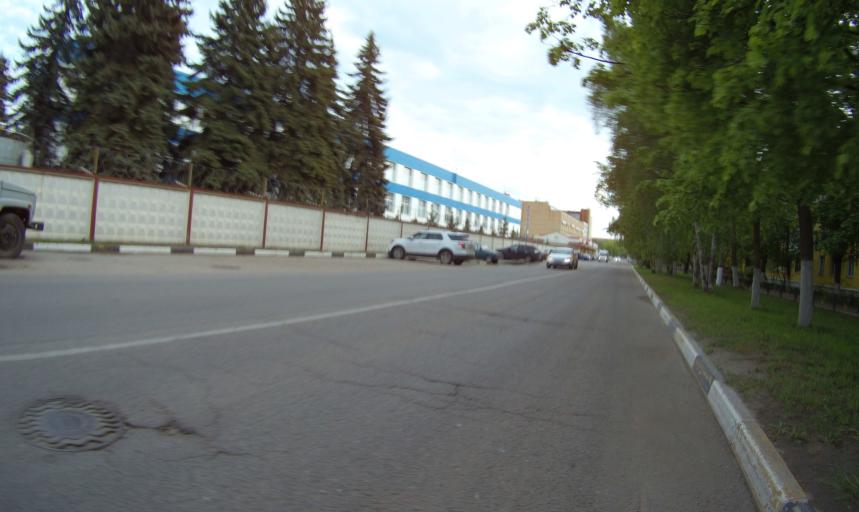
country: RU
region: Moskovskaya
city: Ramenskoye
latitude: 55.5670
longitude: 38.2433
